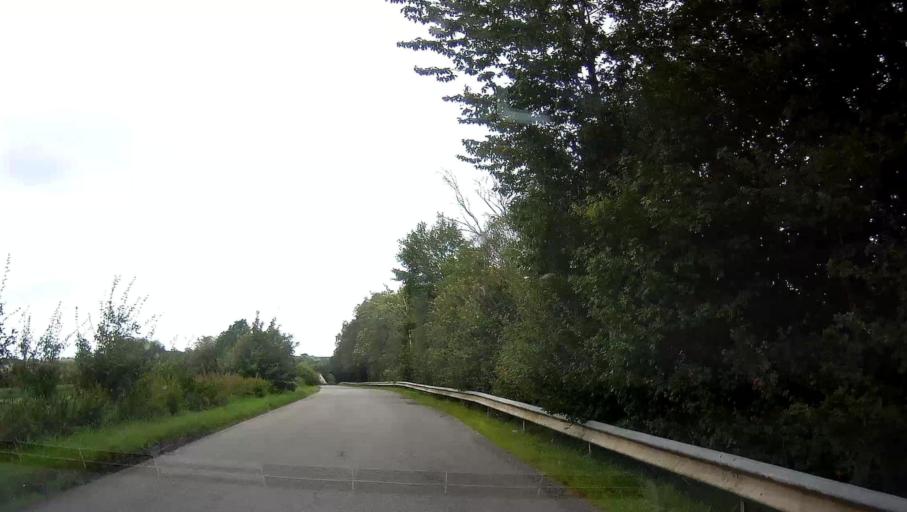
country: BE
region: Wallonia
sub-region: Province de Namur
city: Philippeville
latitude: 50.2334
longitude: 4.5116
